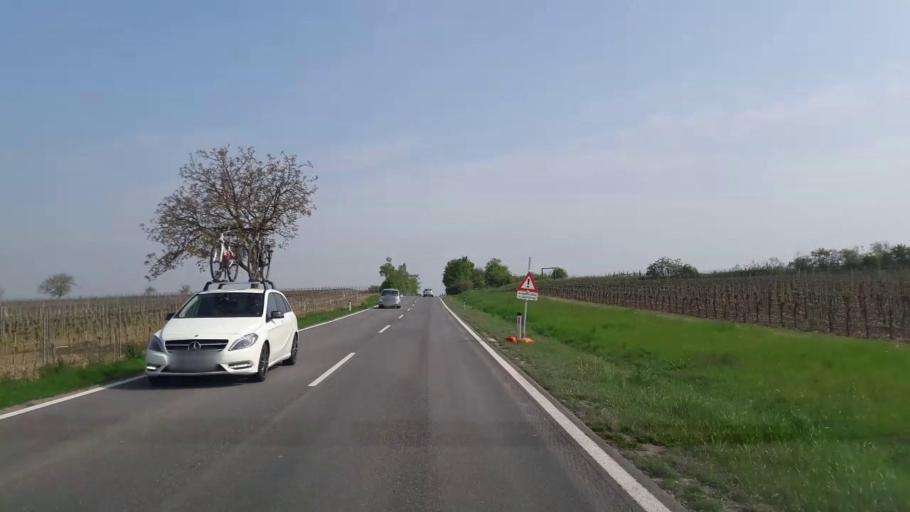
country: AT
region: Lower Austria
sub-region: Politischer Bezirk Hollabrunn
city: Haugsdorf
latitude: 48.6771
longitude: 16.0555
